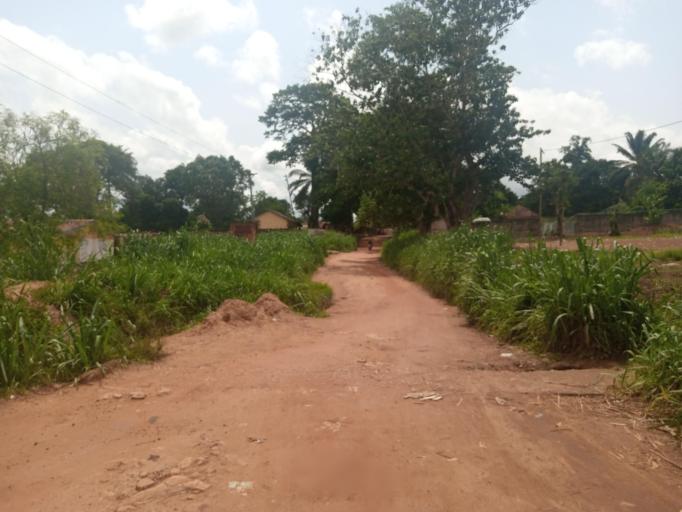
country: SL
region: Southern Province
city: Bo
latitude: 7.9637
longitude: -11.7478
